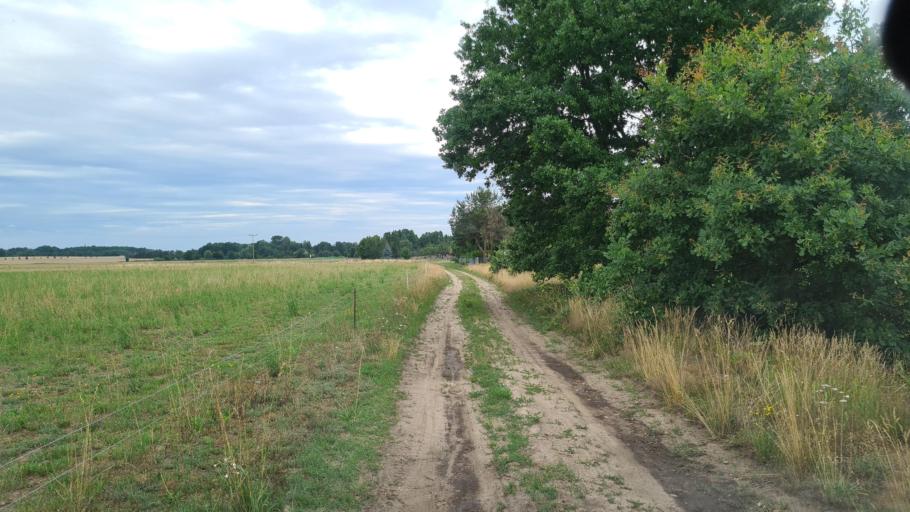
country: DE
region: Brandenburg
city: Crinitz
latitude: 51.7189
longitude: 13.8340
